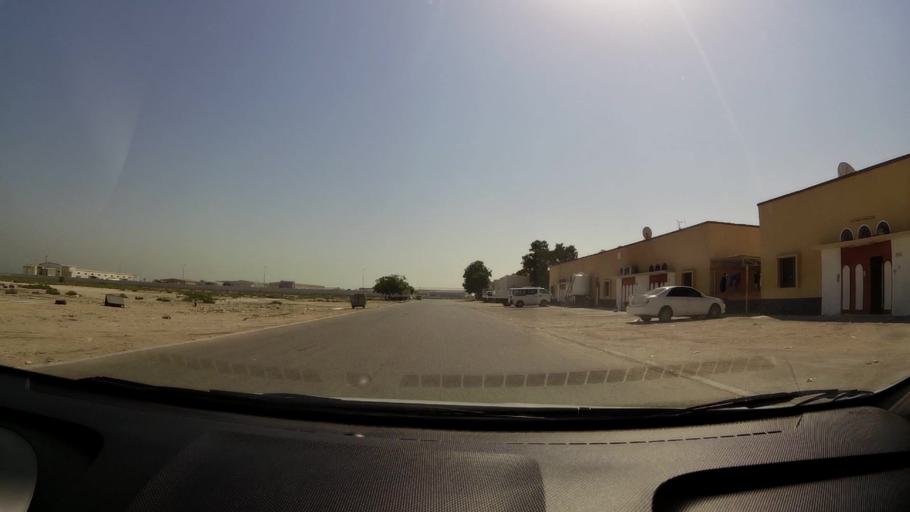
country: AE
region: Umm al Qaywayn
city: Umm al Qaywayn
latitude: 25.5889
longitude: 55.5745
